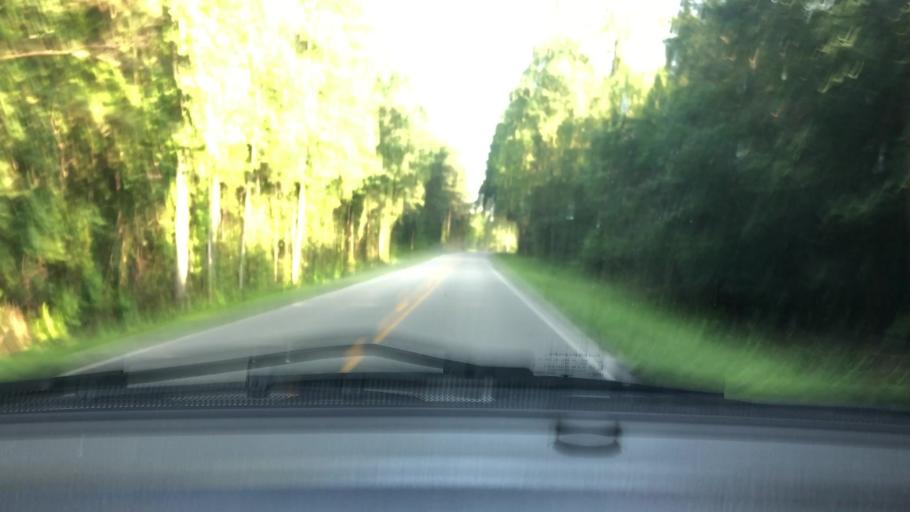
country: US
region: North Carolina
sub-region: Lee County
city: Broadway
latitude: 35.3326
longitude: -79.0724
